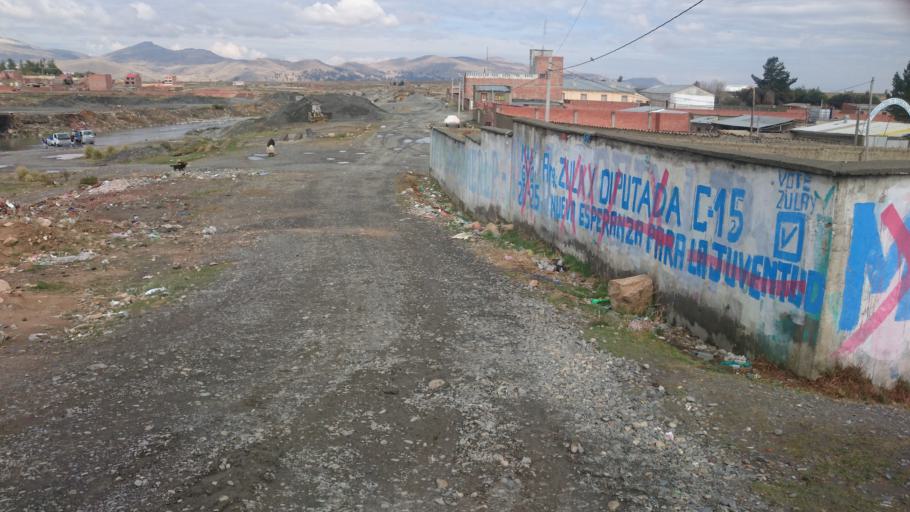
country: BO
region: La Paz
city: Achacachi
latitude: -16.0379
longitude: -68.6869
